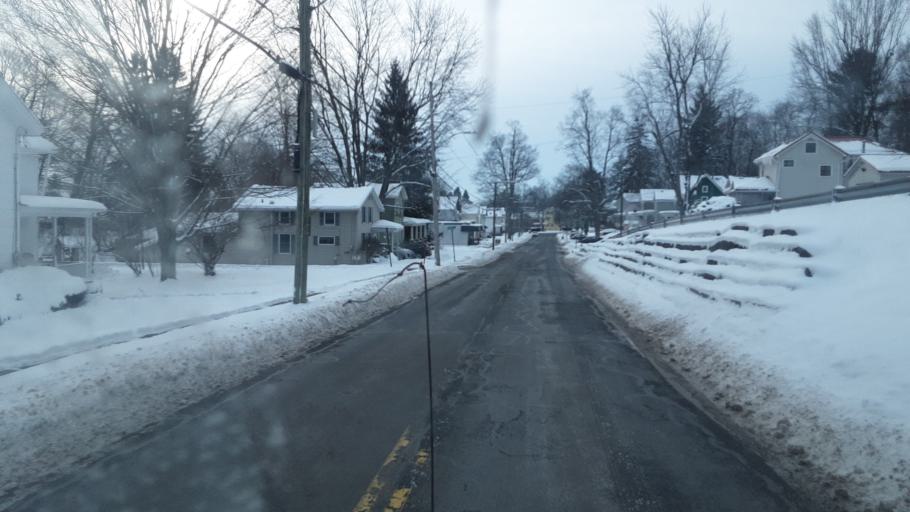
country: US
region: New York
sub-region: Wayne County
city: Lyons
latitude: 43.0718
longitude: -76.9924
